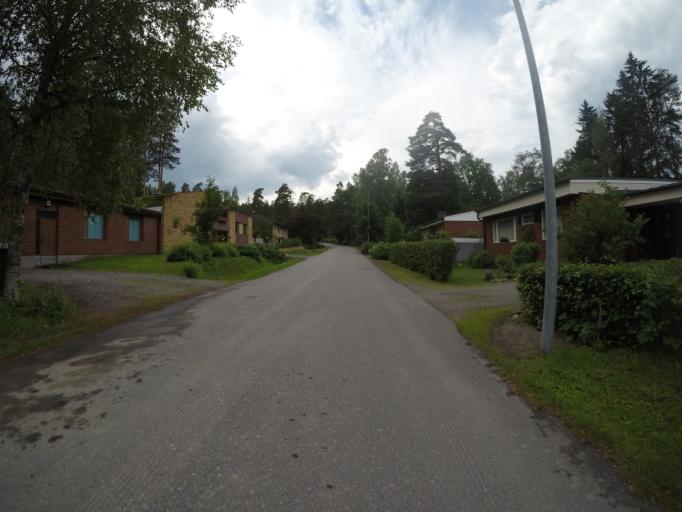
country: FI
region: Haeme
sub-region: Haemeenlinna
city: Haemeenlinna
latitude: 61.0138
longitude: 24.4942
